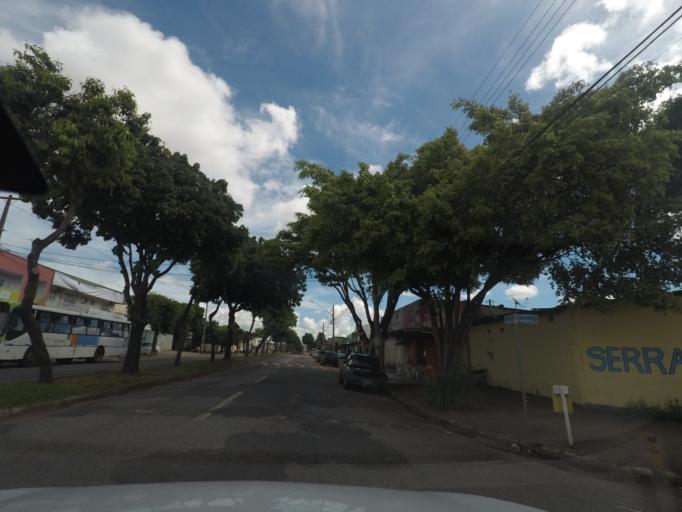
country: BR
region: Goias
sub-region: Goiania
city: Goiania
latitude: -16.7247
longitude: -49.3227
